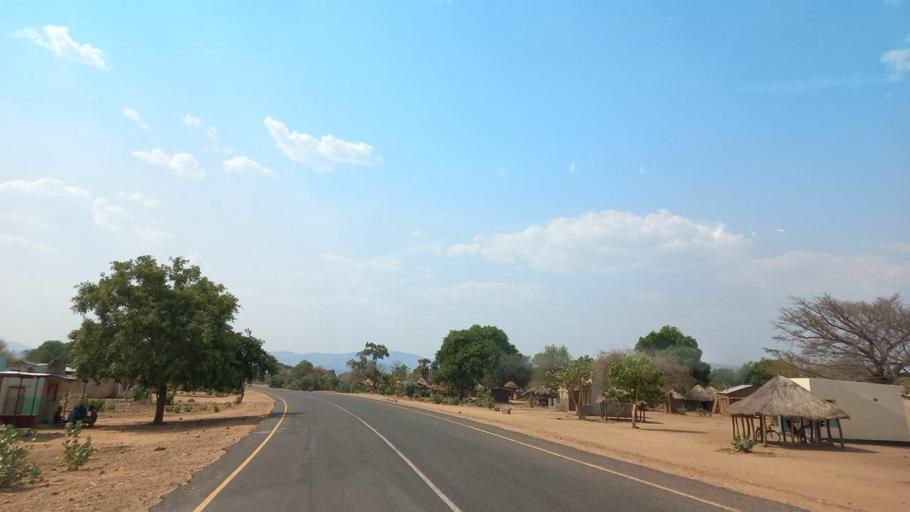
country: ZM
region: Lusaka
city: Luangwa
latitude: -15.1155
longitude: 30.2063
